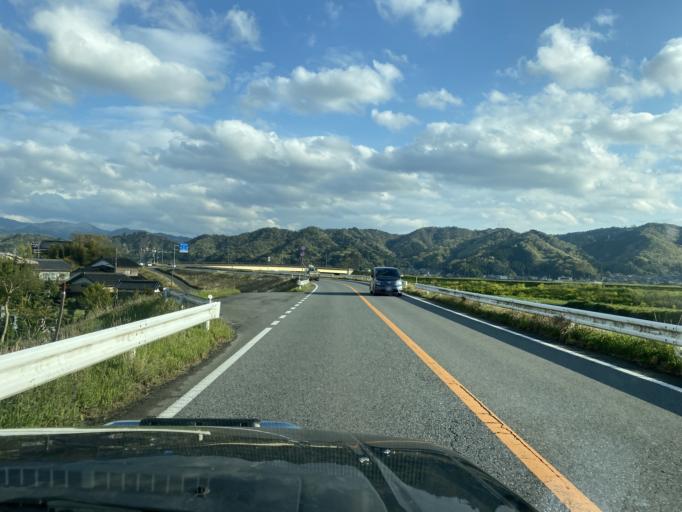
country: JP
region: Hyogo
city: Toyooka
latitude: 35.4944
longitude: 134.8407
